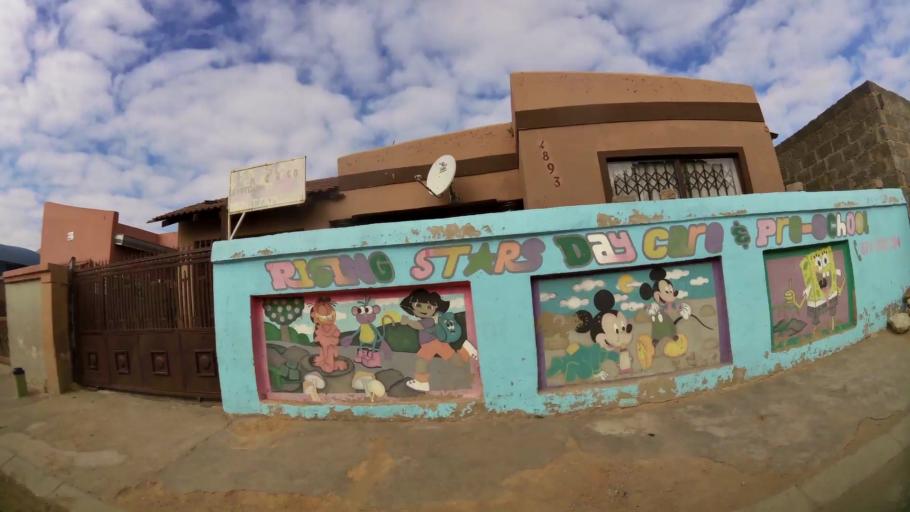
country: ZA
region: Gauteng
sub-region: City of Johannesburg Metropolitan Municipality
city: Modderfontein
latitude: -26.0451
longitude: 28.1842
